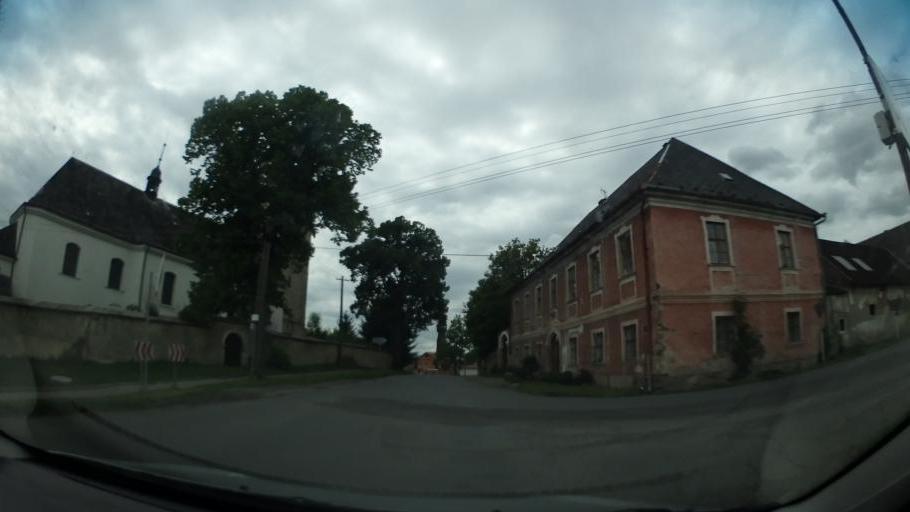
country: CZ
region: Pardubicky
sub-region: Okres Svitavy
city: Moravska Trebova
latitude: 49.7952
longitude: 16.6769
